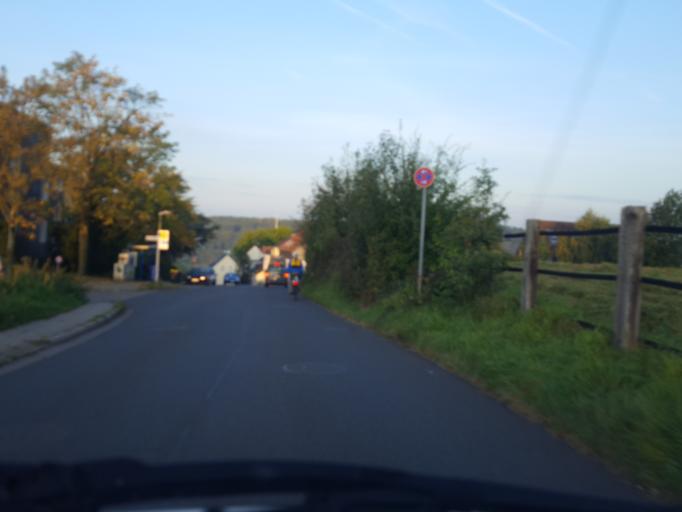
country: DE
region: North Rhine-Westphalia
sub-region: Regierungsbezirk Dusseldorf
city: Velbert
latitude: 51.3918
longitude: 7.0129
